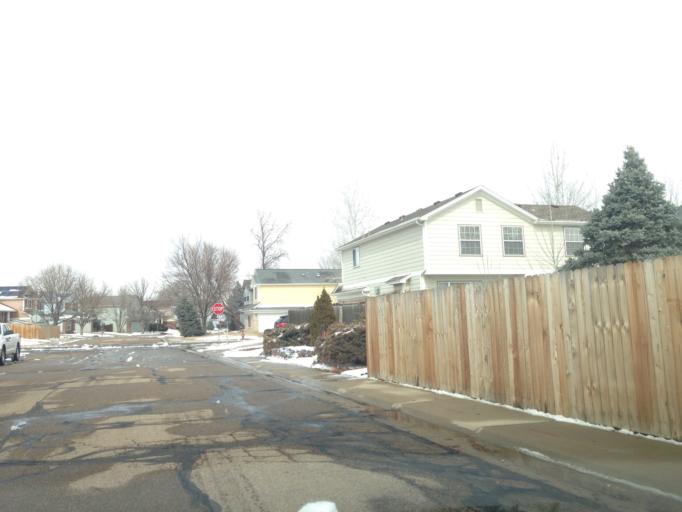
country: US
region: Colorado
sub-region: Boulder County
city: Lafayette
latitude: 39.9731
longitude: -105.0960
